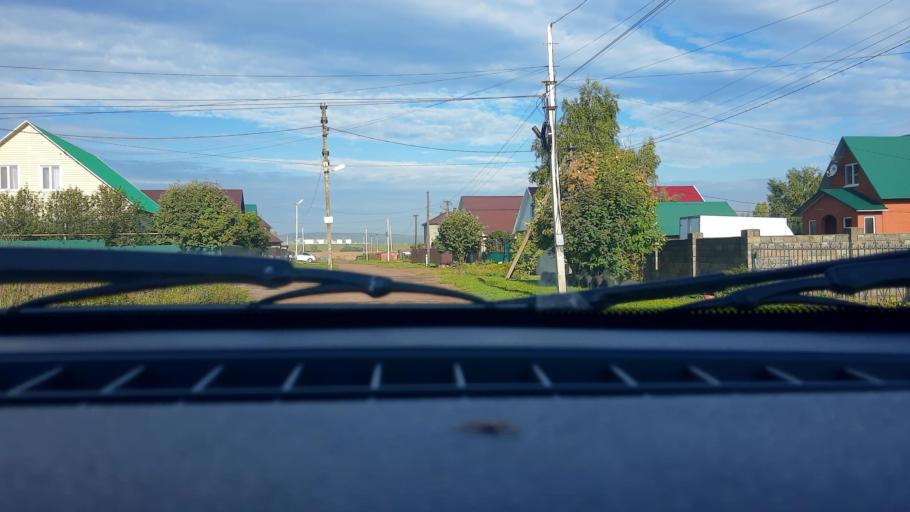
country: RU
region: Bashkortostan
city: Mikhaylovka
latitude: 54.8186
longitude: 55.7916
